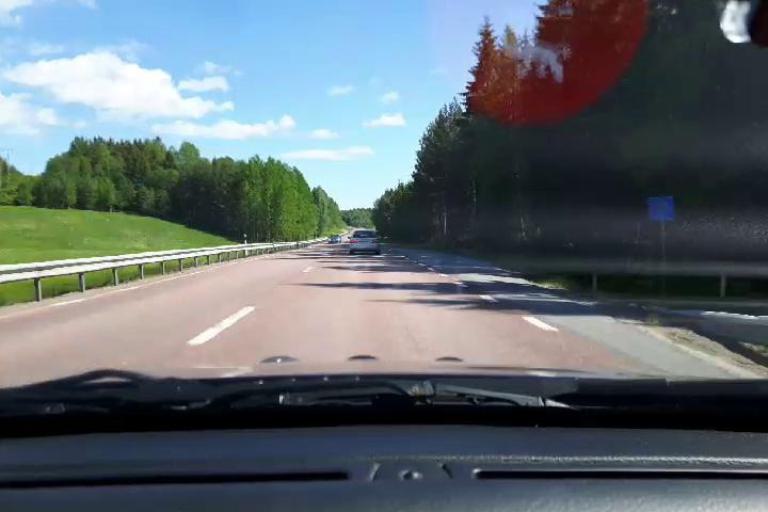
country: SE
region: Gaevleborg
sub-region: Hudiksvalls Kommun
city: Sorforsa
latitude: 61.7463
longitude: 16.8450
